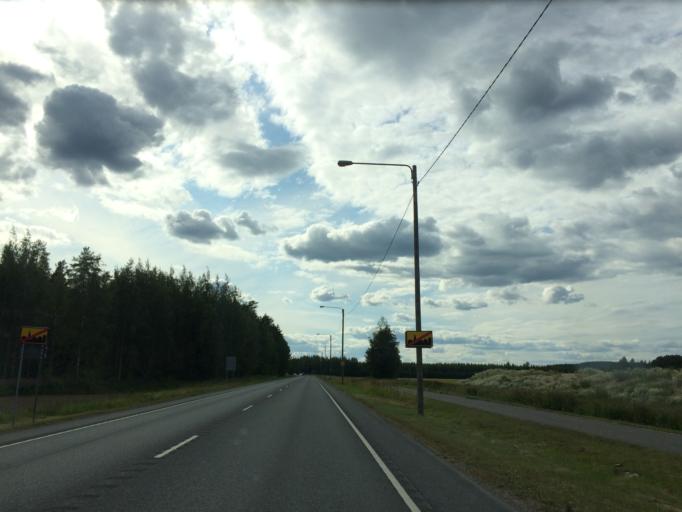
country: FI
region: Haeme
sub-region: Haemeenlinna
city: Janakkala
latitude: 60.9214
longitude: 24.6062
